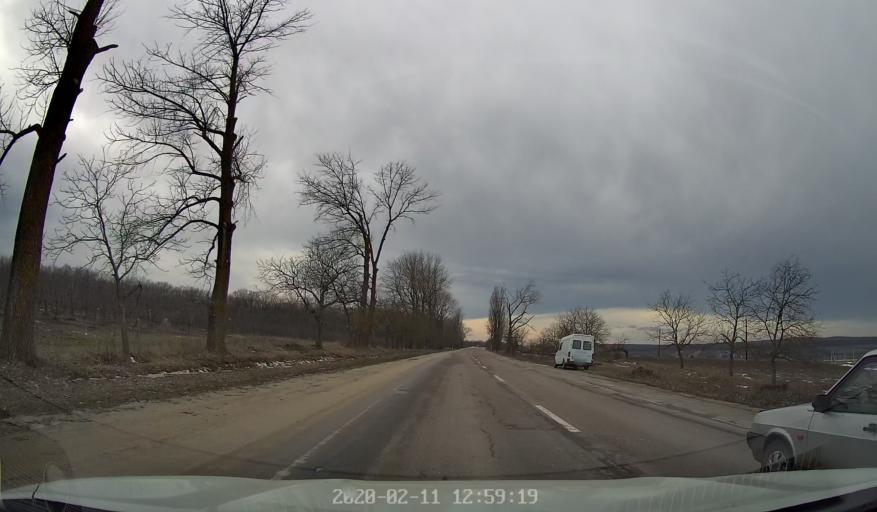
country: MD
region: Briceni
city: Briceni
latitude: 48.3292
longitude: 27.0383
